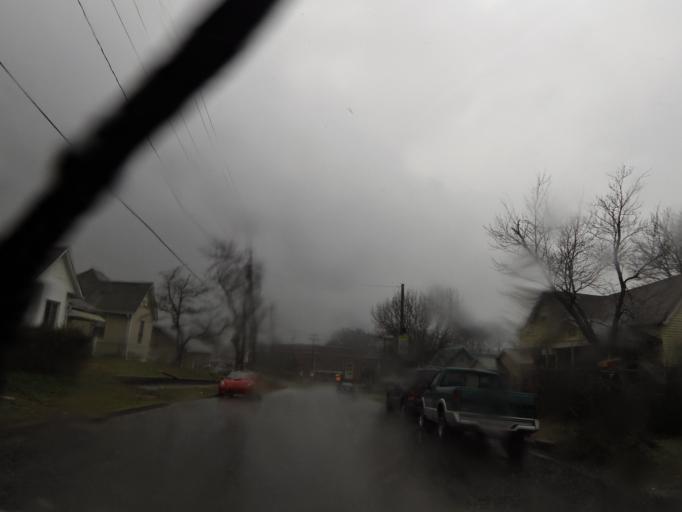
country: US
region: Tennessee
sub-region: Knox County
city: Knoxville
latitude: 35.9844
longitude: -83.9529
